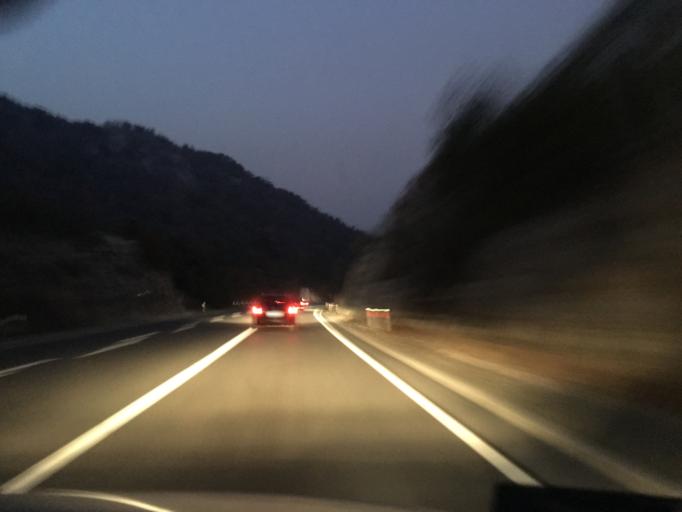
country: ME
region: Cetinje
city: Cetinje
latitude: 42.3780
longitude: 19.0467
